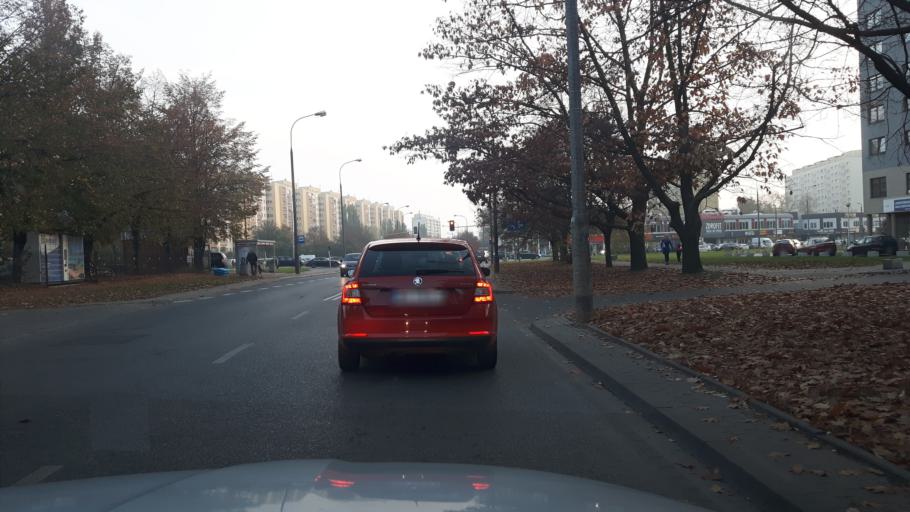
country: PL
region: Masovian Voivodeship
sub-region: Warszawa
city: Mokotow
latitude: 52.1809
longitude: 21.0142
